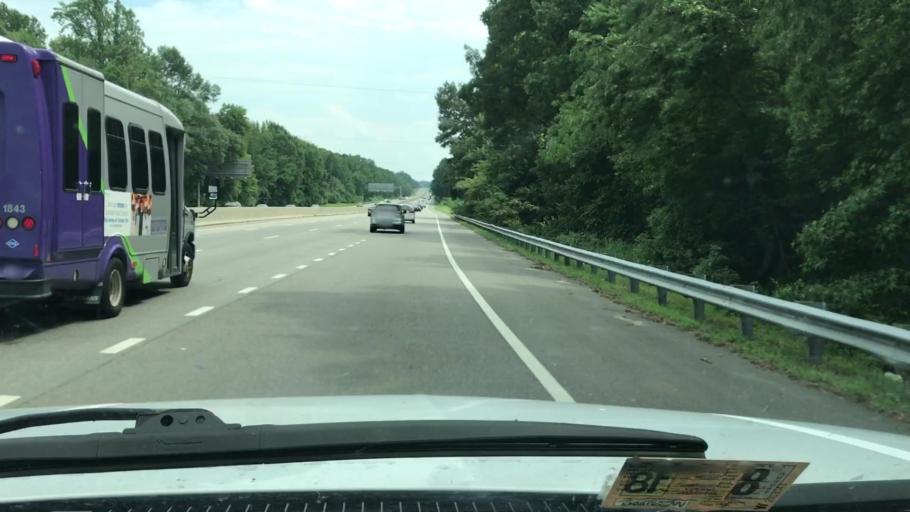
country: US
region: Virginia
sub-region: Chesterfield County
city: Bon Air
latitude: 37.4985
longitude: -77.5239
